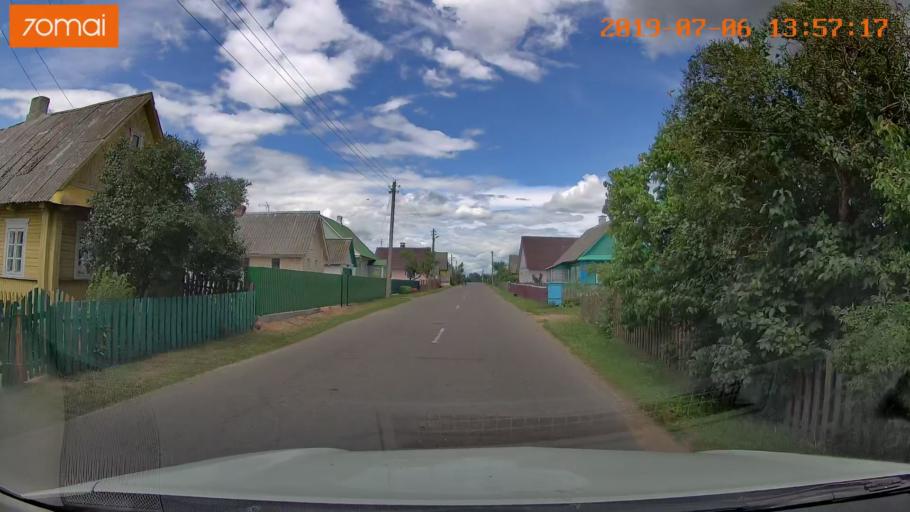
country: BY
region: Minsk
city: Ivyanyets
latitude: 53.7729
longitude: 26.8060
